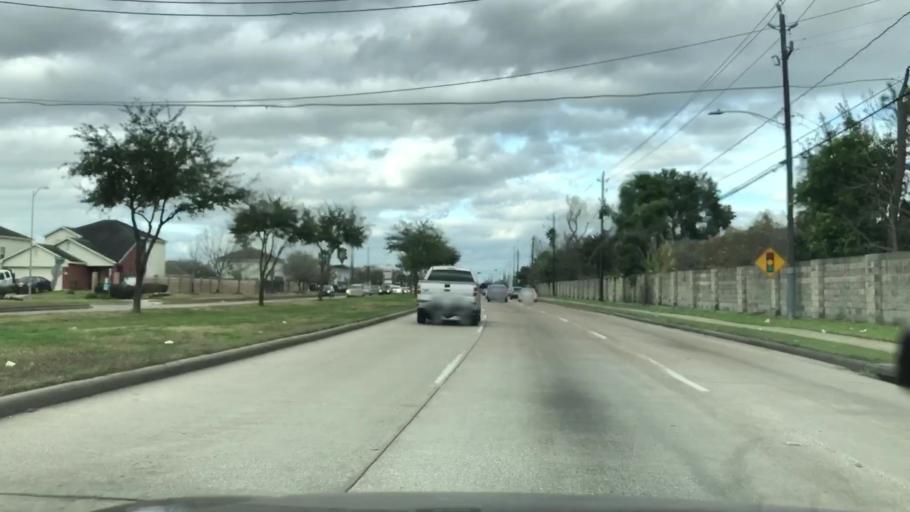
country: US
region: Texas
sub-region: Harris County
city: Bellaire
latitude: 29.6324
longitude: -95.4634
